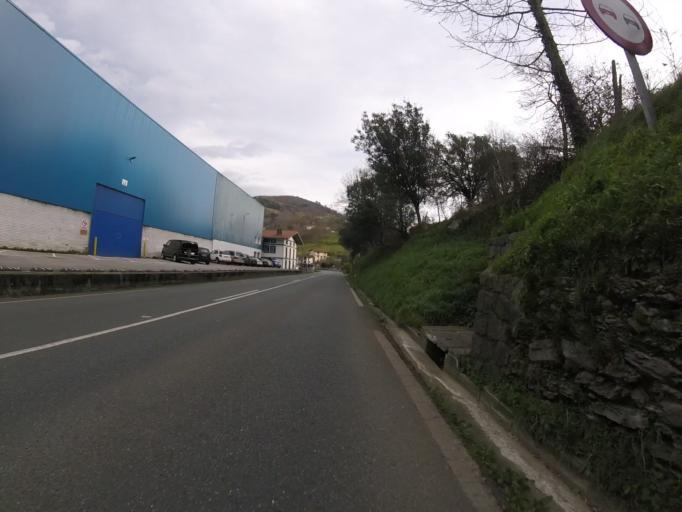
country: ES
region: Basque Country
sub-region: Provincia de Guipuzcoa
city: Aizarnazabal
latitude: 43.2522
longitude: -2.2369
